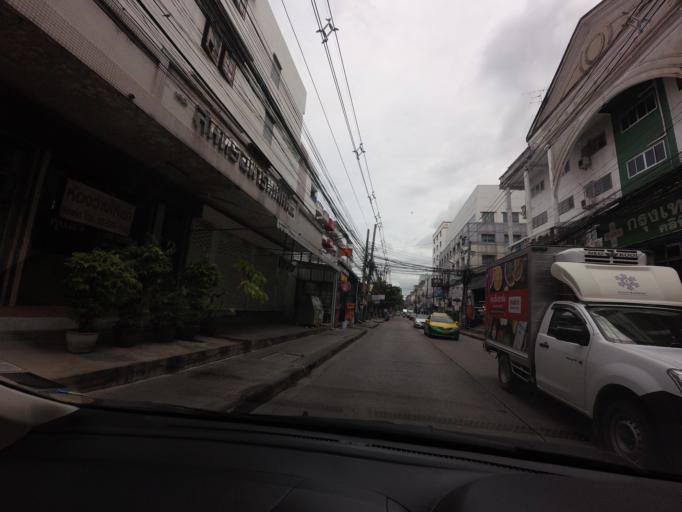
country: TH
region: Bangkok
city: Wang Thonglang
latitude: 13.7675
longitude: 100.6232
